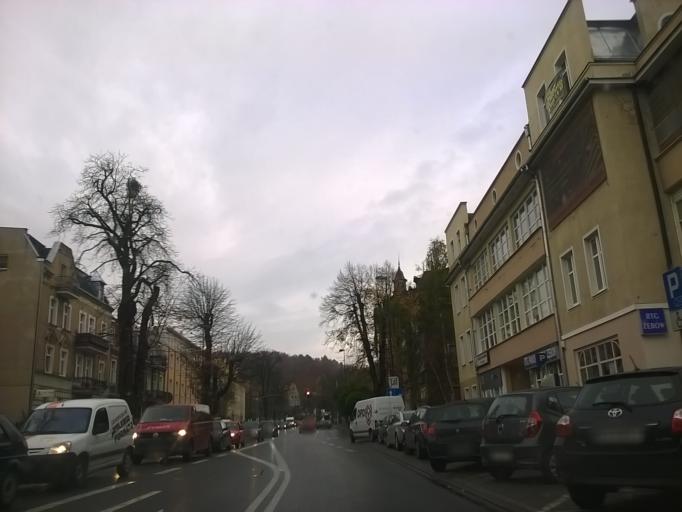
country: PL
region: Pomeranian Voivodeship
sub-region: Gdansk
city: Gdansk
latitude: 54.3761
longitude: 18.6070
